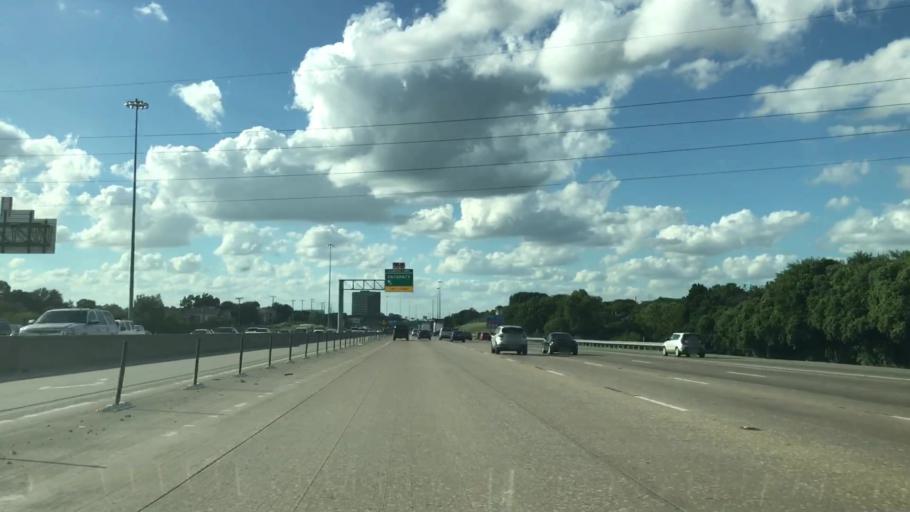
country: US
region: Texas
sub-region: Dallas County
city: Richardson
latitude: 32.9023
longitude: -96.7206
